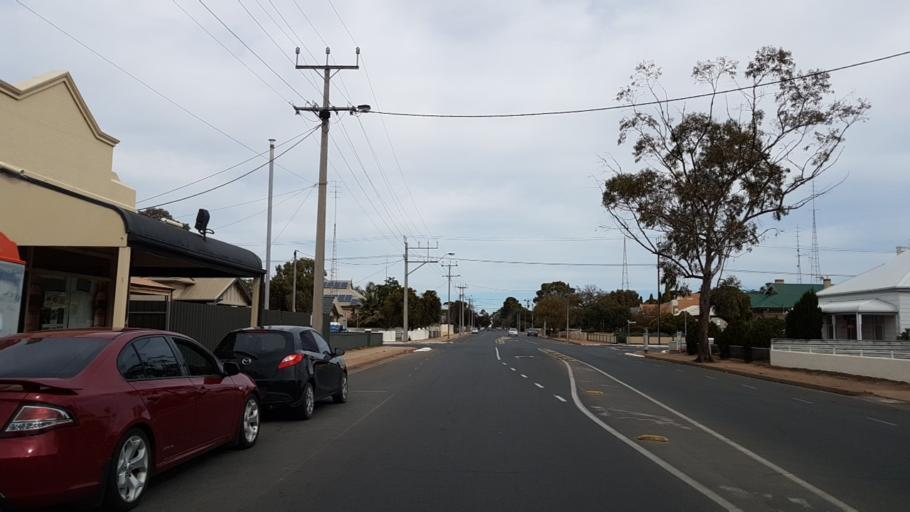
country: AU
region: South Australia
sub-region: Port Pirie City and Dists
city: Port Pirie
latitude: -33.1928
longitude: 138.0039
